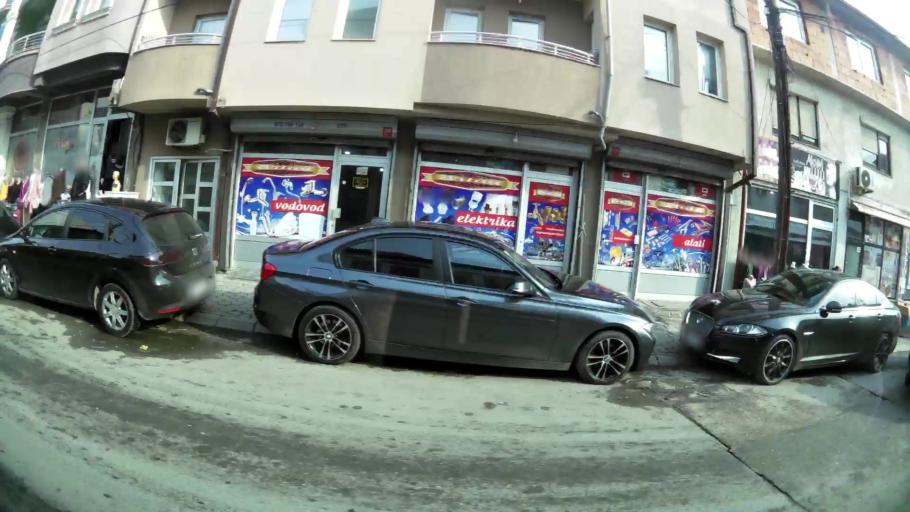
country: MK
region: Karpos
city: Skopje
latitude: 42.0065
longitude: 21.4350
